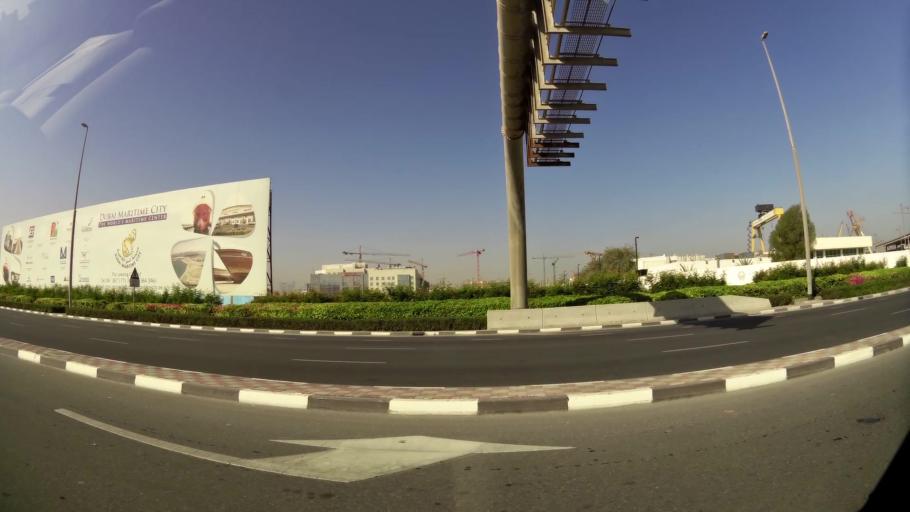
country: AE
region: Ash Shariqah
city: Sharjah
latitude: 25.2506
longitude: 55.2791
